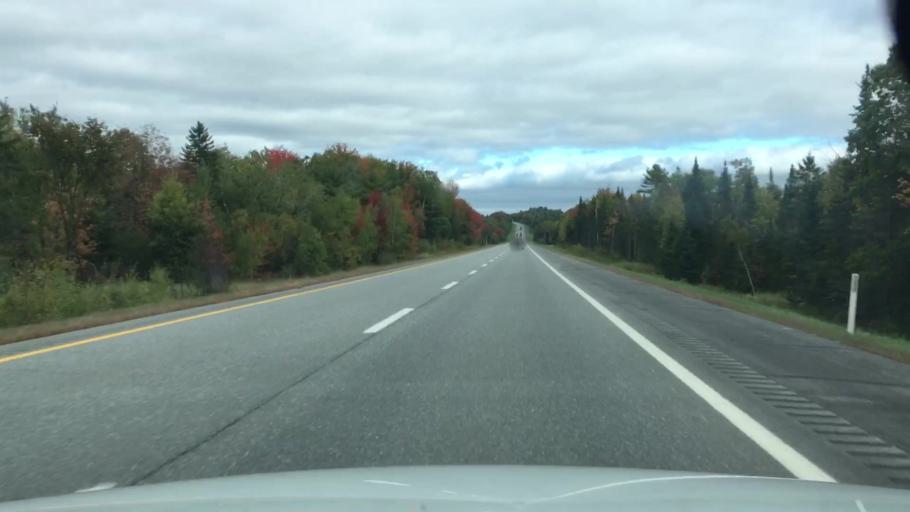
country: US
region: Maine
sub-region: Penobscot County
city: Carmel
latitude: 44.7768
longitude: -69.0529
